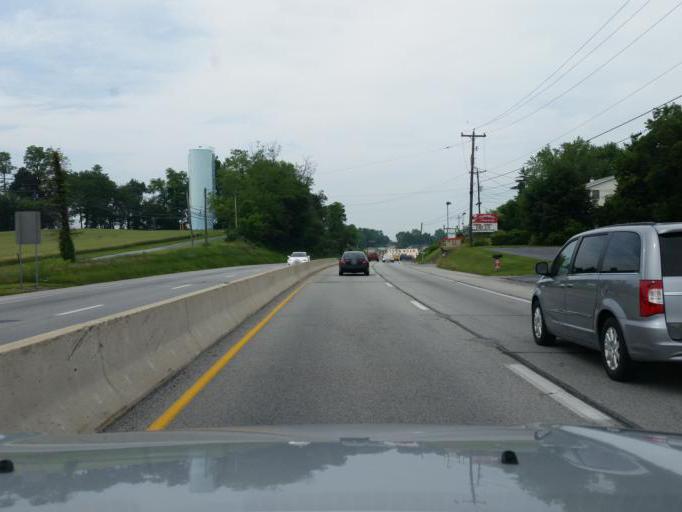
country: US
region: Pennsylvania
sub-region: York County
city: Dillsburg
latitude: 40.1274
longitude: -77.0231
